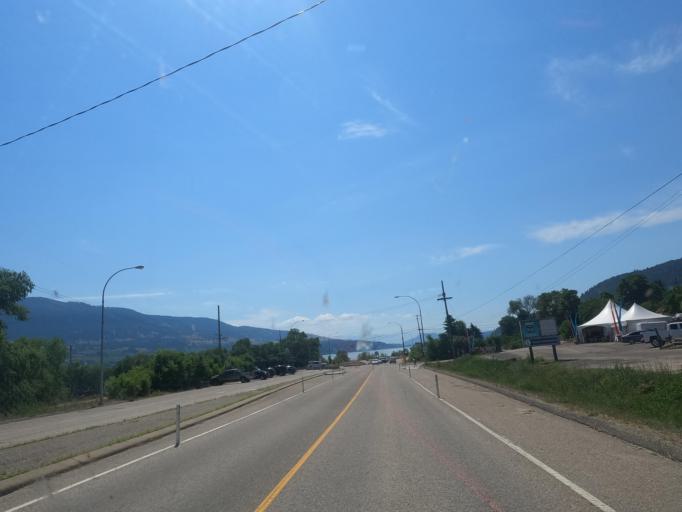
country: CA
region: British Columbia
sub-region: Regional District of North Okanagan
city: Vernon
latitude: 50.1116
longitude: -119.3877
